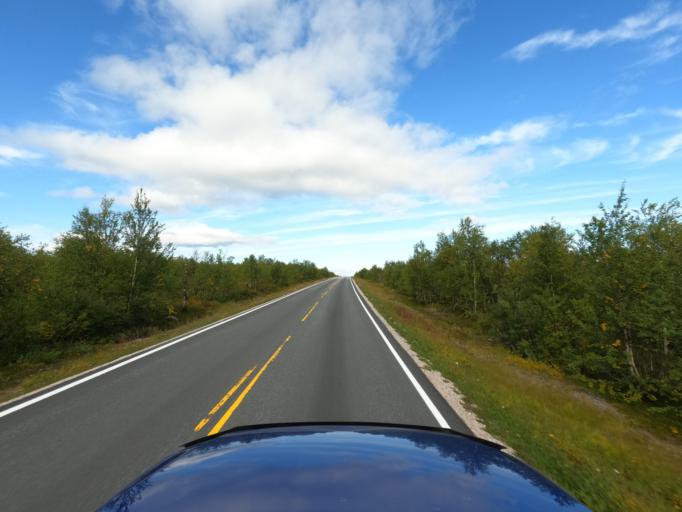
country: NO
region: Finnmark Fylke
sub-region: Karasjok
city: Karasjohka
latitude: 69.6451
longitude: 25.2816
